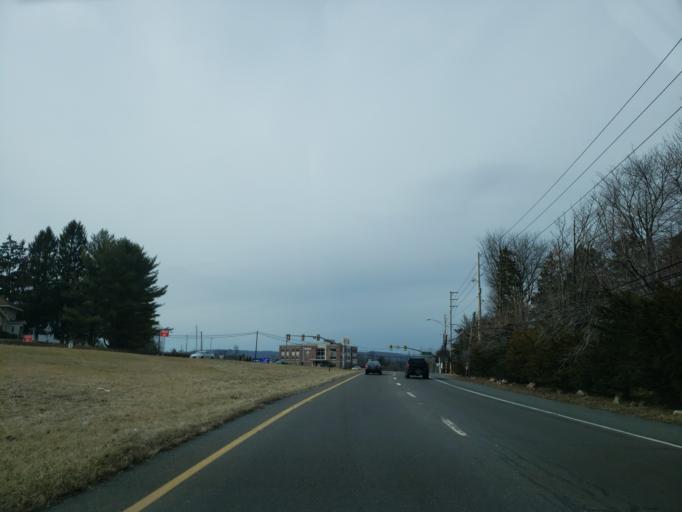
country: US
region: Pennsylvania
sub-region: Lehigh County
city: Coopersburg
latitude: 40.5326
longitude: -75.4036
